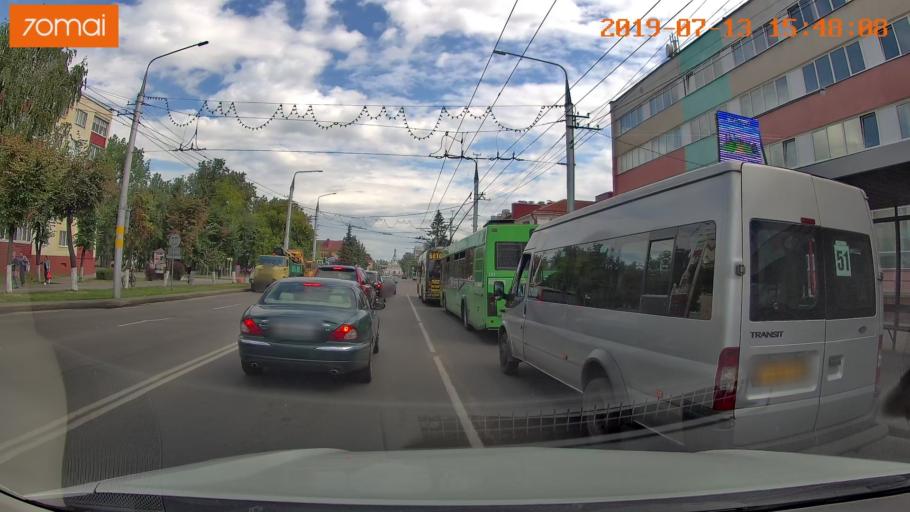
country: BY
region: Mogilev
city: Babruysk
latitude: 53.1487
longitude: 29.2298
